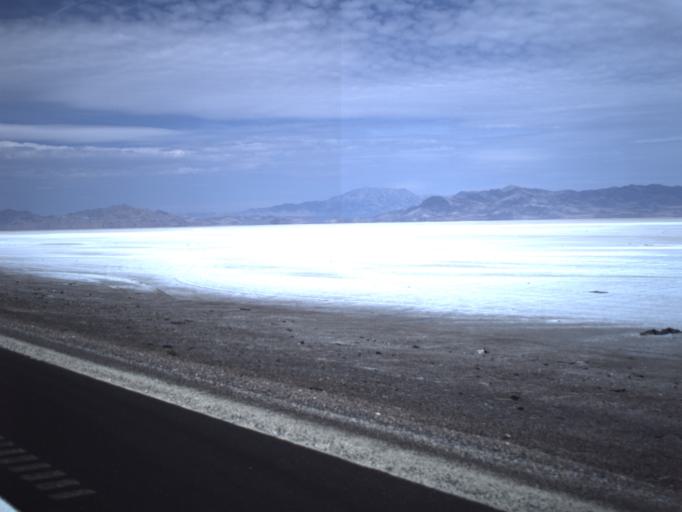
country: US
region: Utah
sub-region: Tooele County
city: Wendover
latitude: 40.7349
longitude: -113.6341
